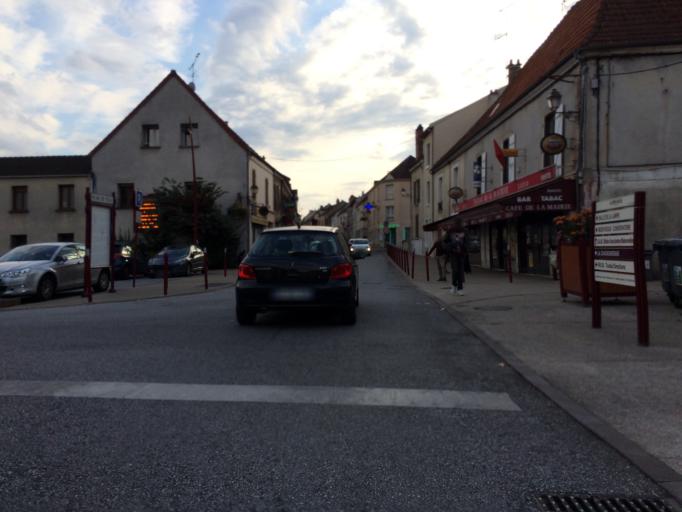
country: FR
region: Ile-de-France
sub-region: Departement de l'Essonne
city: Linas
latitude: 48.6318
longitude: 2.2662
